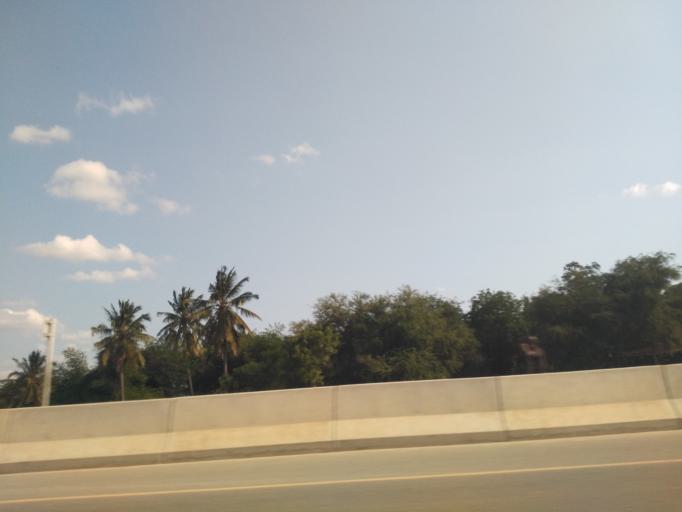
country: TZ
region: Dar es Salaam
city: Dar es Salaam
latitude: -6.8590
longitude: 39.2921
